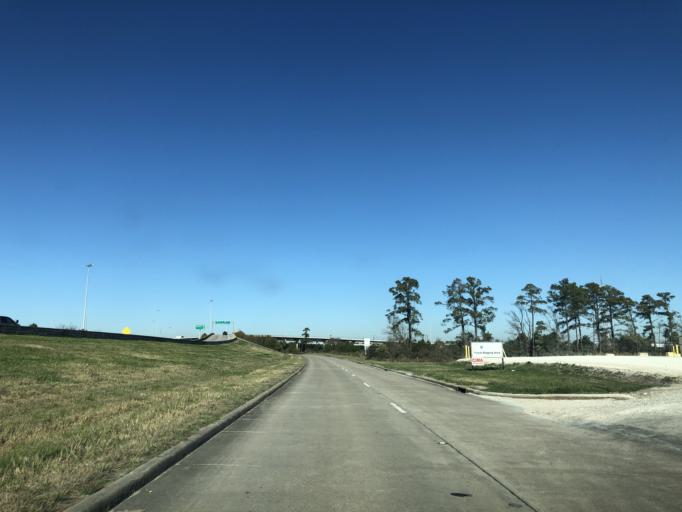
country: US
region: Texas
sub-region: Harris County
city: Cloverleaf
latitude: 29.7643
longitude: -95.1469
